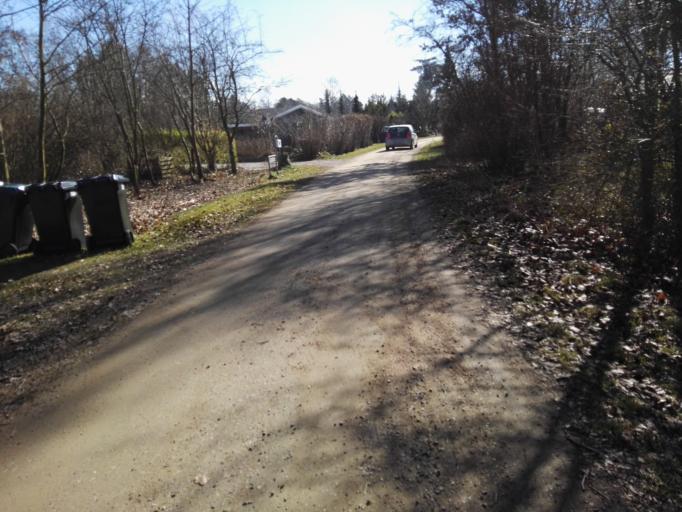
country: DK
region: Zealand
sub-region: Lejre Kommune
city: Ejby
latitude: 55.7799
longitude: 11.8046
